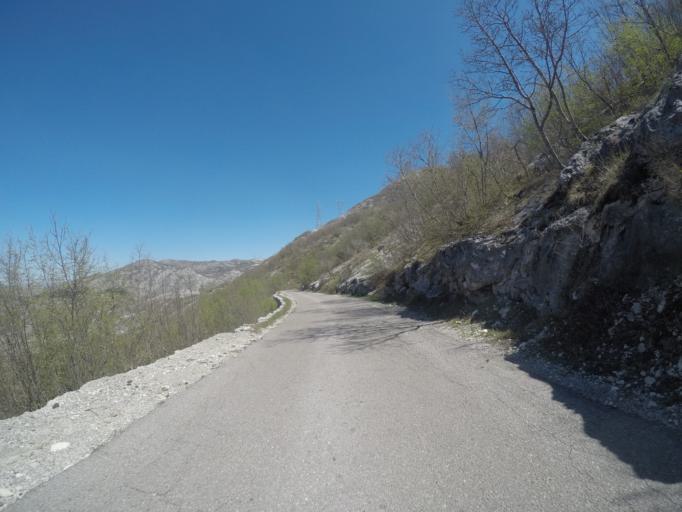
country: ME
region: Cetinje
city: Cetinje
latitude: 42.4477
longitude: 18.8732
